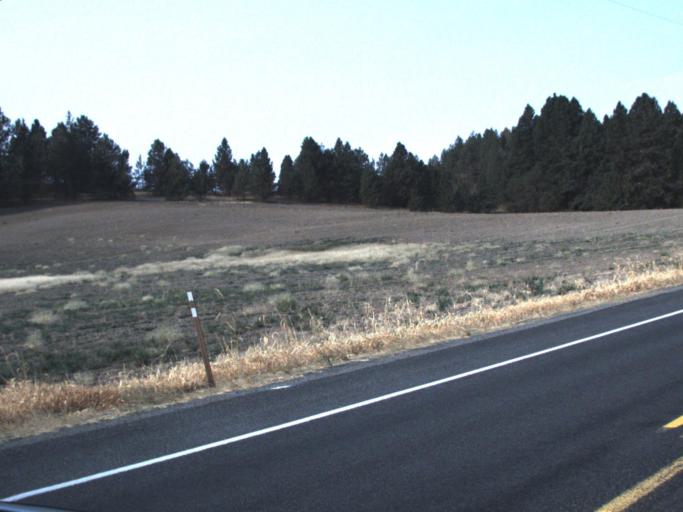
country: US
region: Idaho
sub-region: Benewah County
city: Plummer
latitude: 47.4357
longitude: -117.0476
